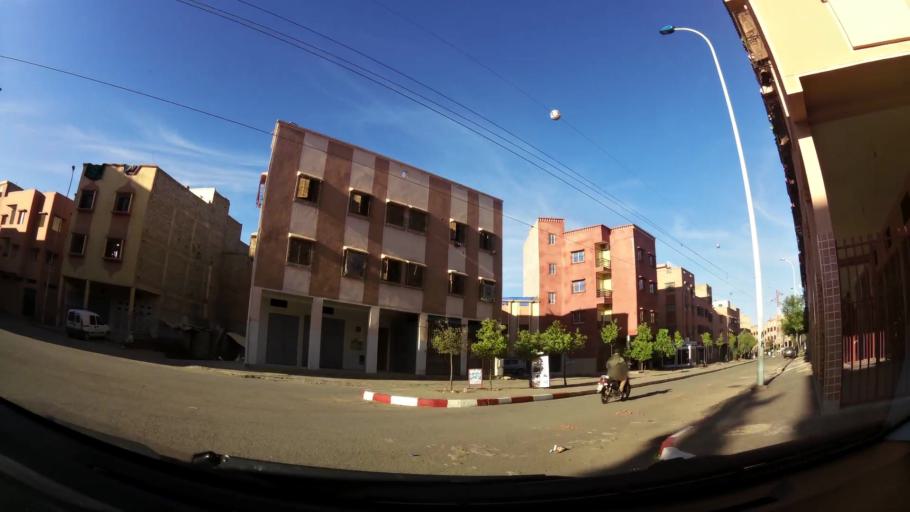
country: MA
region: Marrakech-Tensift-Al Haouz
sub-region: Marrakech
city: Marrakesh
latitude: 31.6150
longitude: -8.0638
